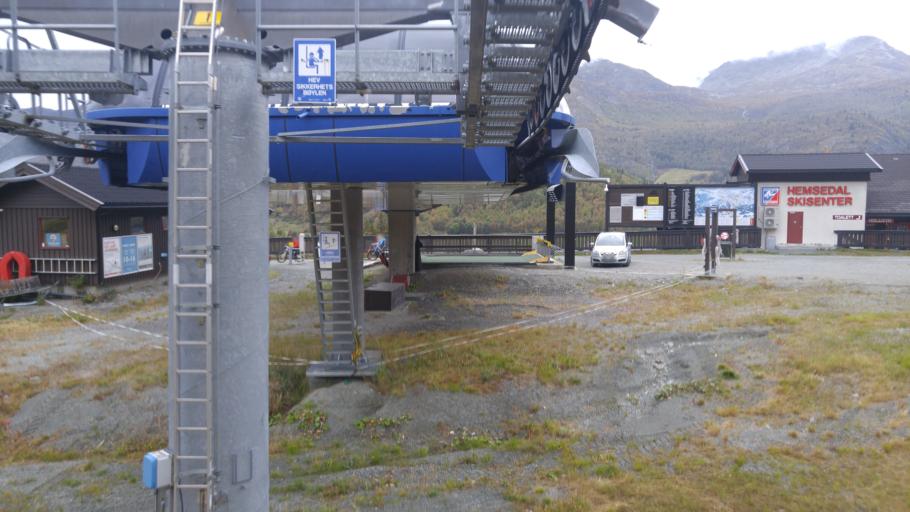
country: NO
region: Buskerud
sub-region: Hemsedal
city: Hemsedal
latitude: 60.8598
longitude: 8.5134
